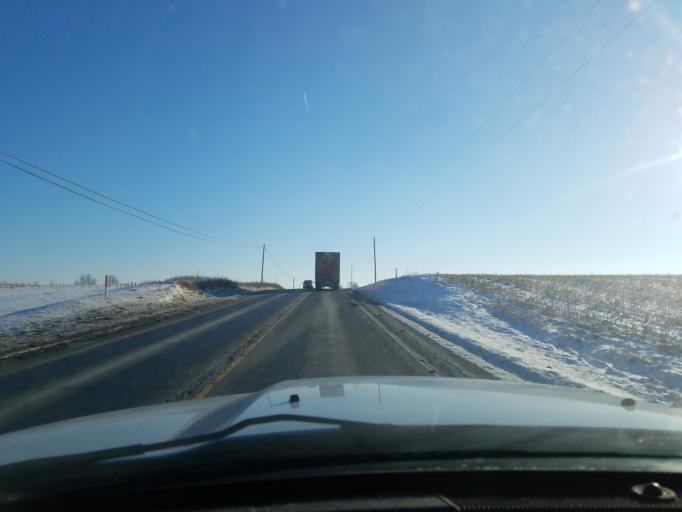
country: US
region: Indiana
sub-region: Noble County
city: Kendallville
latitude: 41.4525
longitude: -85.3234
